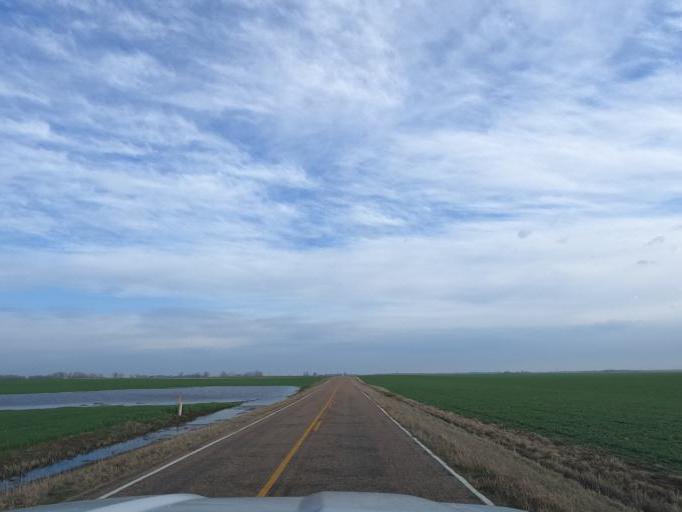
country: US
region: Kansas
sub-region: Rice County
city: Sterling
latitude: 38.0584
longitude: -98.2521
